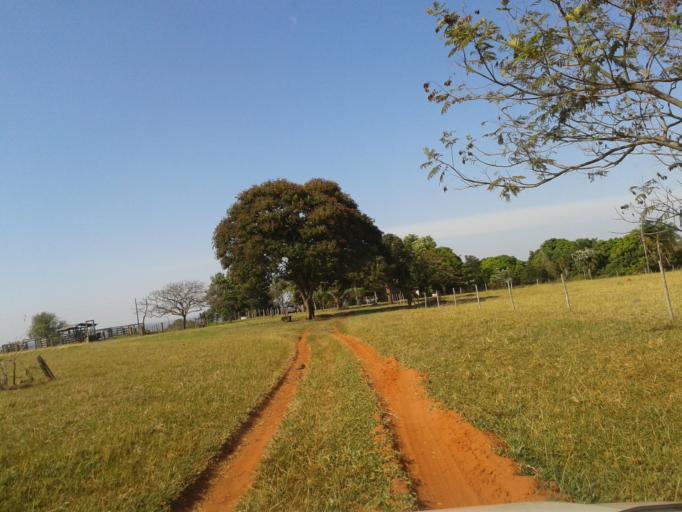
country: BR
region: Minas Gerais
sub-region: Campina Verde
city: Campina Verde
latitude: -19.4578
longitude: -49.6745
